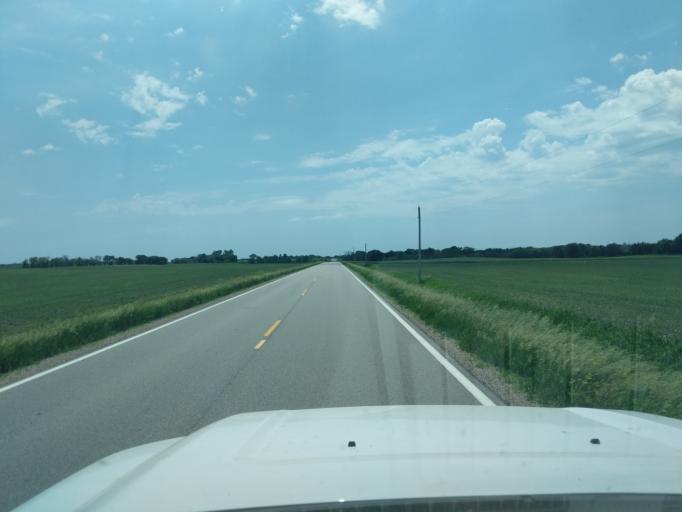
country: US
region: Minnesota
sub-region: Yellow Medicine County
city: Granite Falls
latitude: 44.7557
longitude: -95.4014
